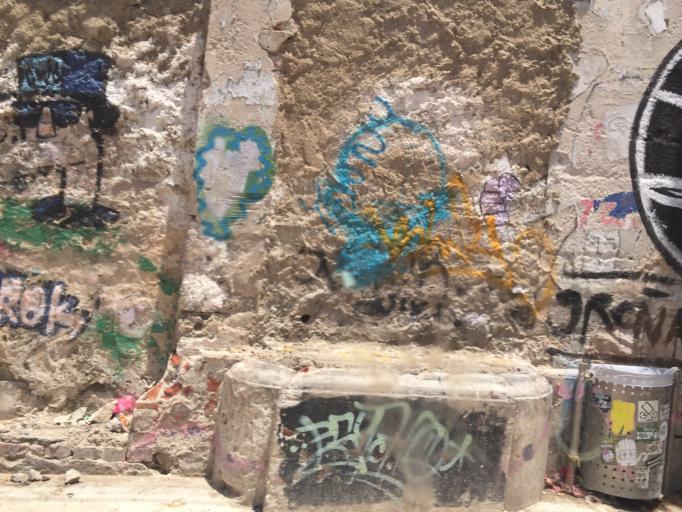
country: CO
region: Bolivar
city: Cartagena
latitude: 10.4210
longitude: -75.5460
